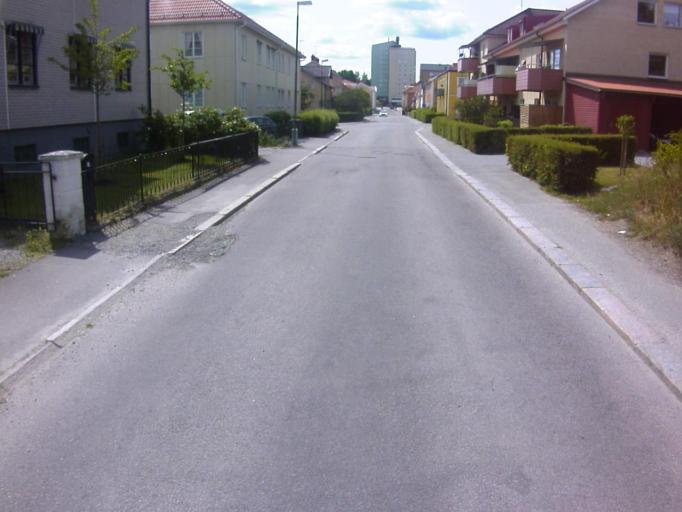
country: SE
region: Soedermanland
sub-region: Eskilstuna Kommun
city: Eskilstuna
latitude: 59.3627
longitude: 16.5192
